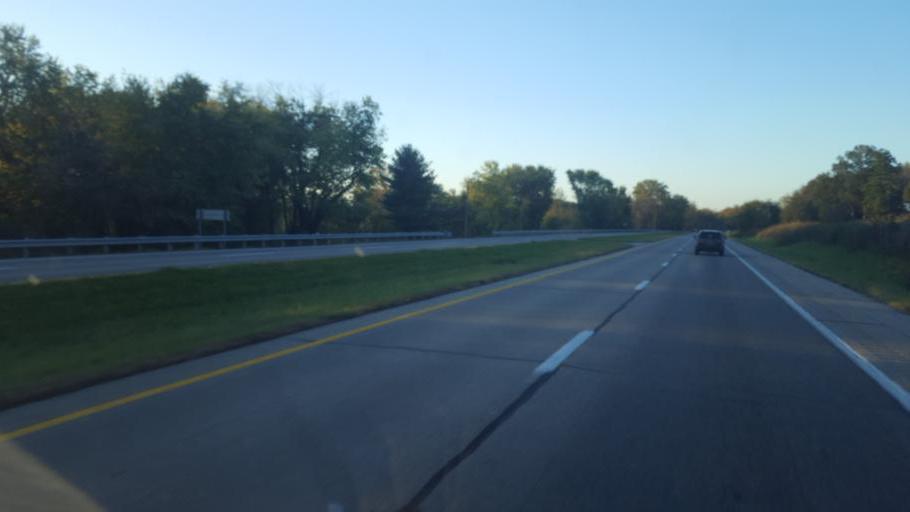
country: US
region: Ohio
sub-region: Scioto County
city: Lucasville
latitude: 38.9279
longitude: -83.0211
